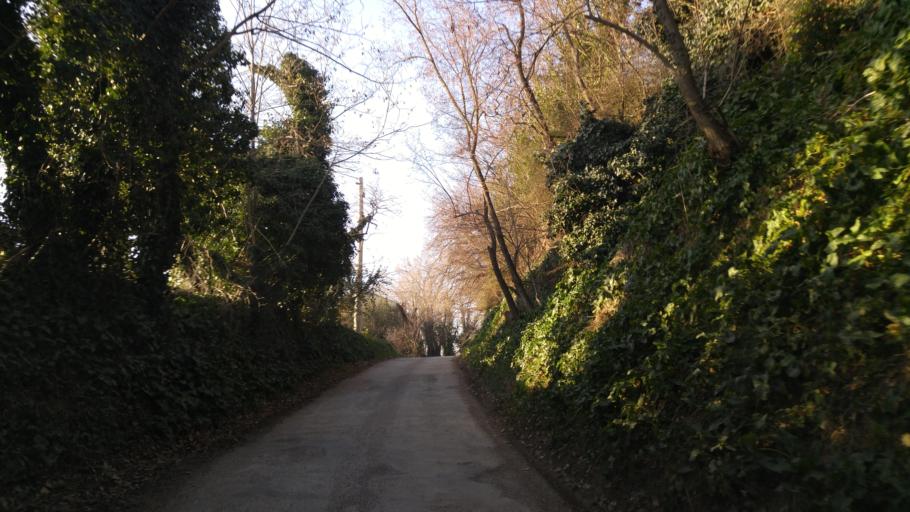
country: IT
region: The Marches
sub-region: Provincia di Pesaro e Urbino
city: Fenile
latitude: 43.8603
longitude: 12.9665
